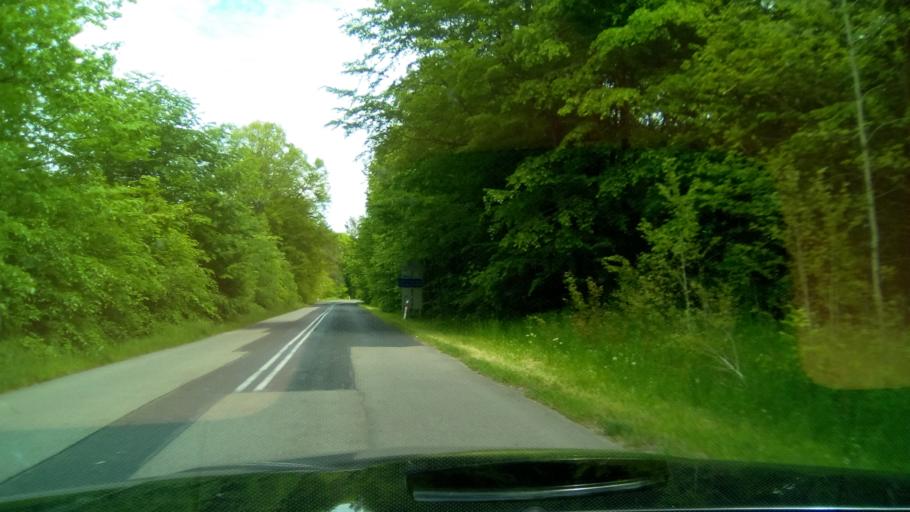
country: PL
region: Pomeranian Voivodeship
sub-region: Powiat leborski
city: Cewice
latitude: 54.3839
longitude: 17.6614
